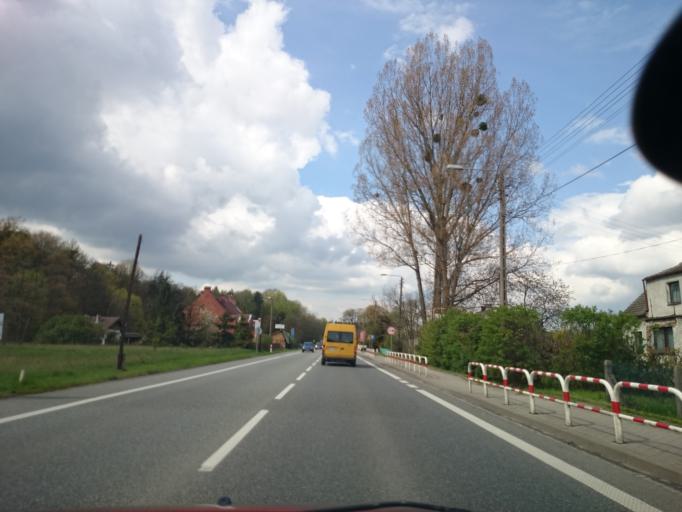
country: PL
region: Opole Voivodeship
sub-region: Powiat opolski
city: Tarnow Opolski
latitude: 50.6028
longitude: 18.0789
